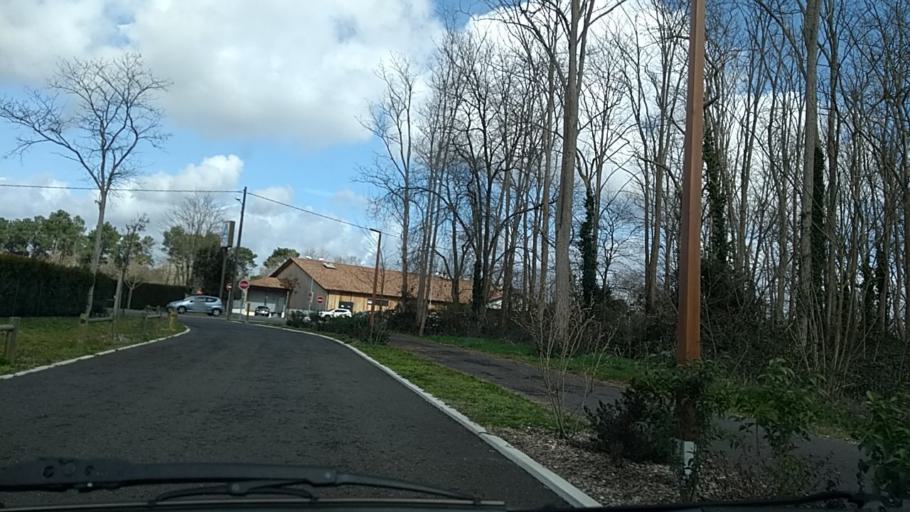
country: FR
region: Aquitaine
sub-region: Departement de la Gironde
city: Salles
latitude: 44.5474
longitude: -0.8775
